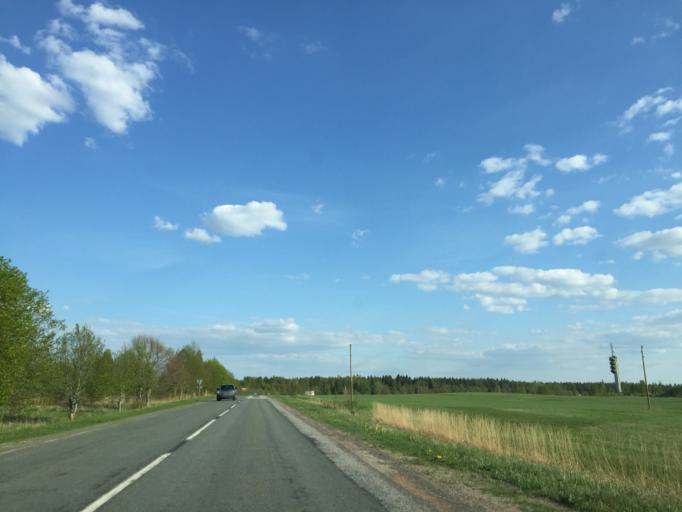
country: LV
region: Sigulda
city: Sigulda
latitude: 57.2584
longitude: 24.8693
